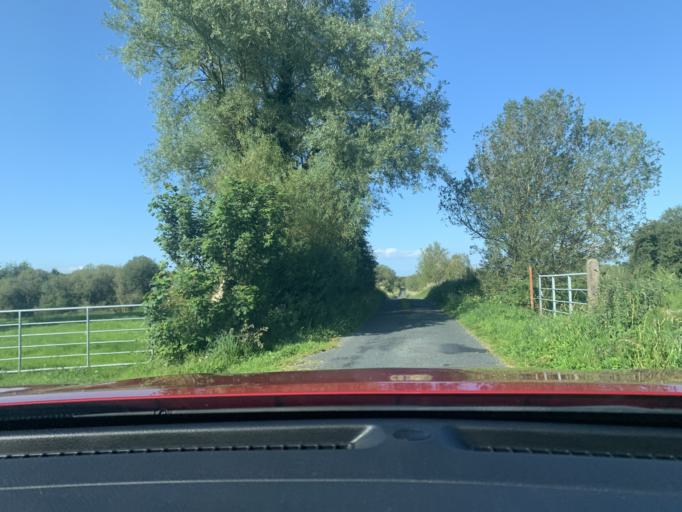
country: IE
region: Connaught
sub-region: Sligo
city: Tobercurry
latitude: 54.0658
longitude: -8.7803
